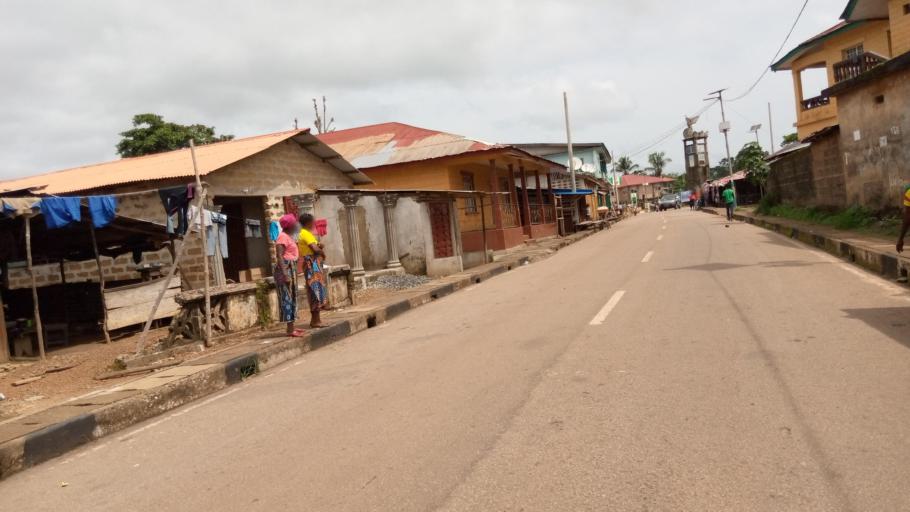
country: SL
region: Southern Province
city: Moyamba
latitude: 8.1592
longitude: -12.4323
